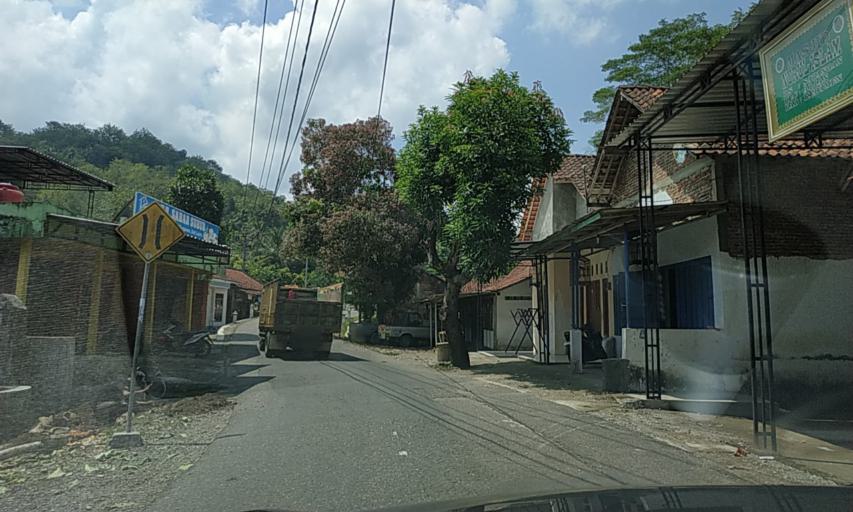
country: ID
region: Central Java
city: Gombong
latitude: -7.6331
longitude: 109.7084
